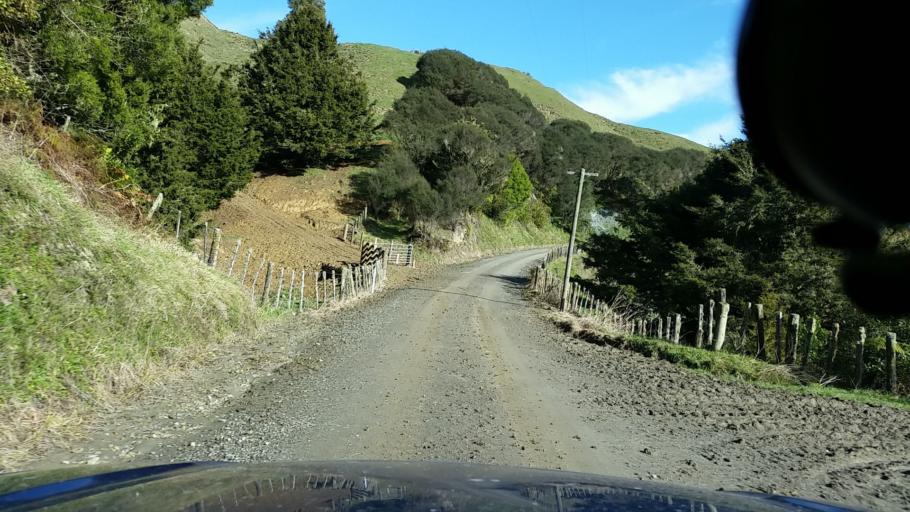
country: NZ
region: Taranaki
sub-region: New Plymouth District
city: Waitara
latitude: -39.0508
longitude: 174.7617
